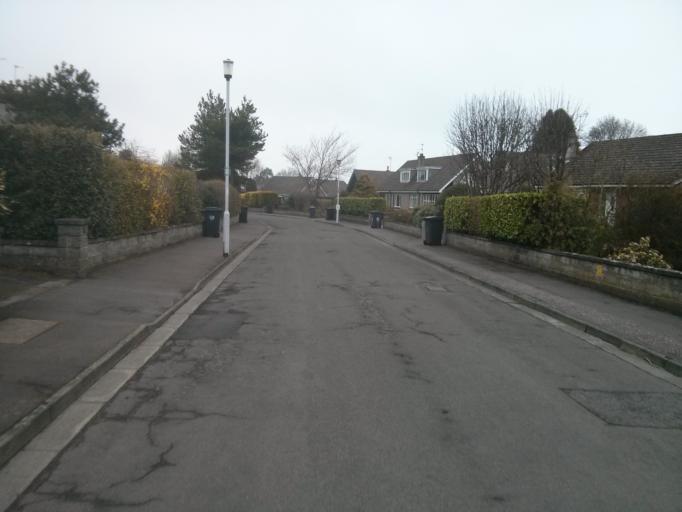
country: GB
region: Scotland
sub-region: Fife
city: Saint Andrews
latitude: 56.3324
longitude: -2.8056
